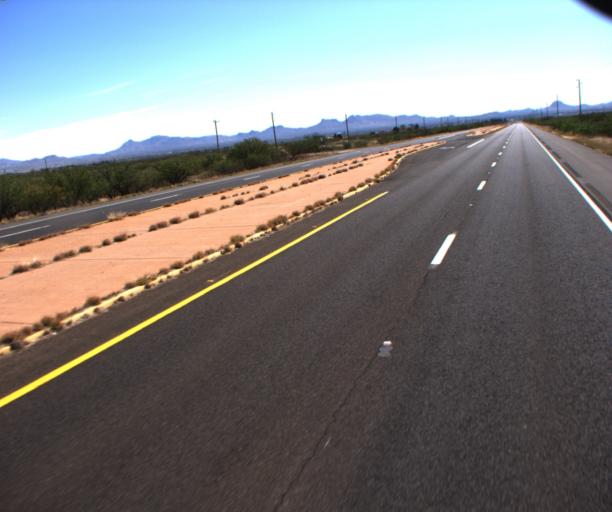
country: US
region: Arizona
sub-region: Cochise County
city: Pirtleville
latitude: 31.3596
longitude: -109.6543
